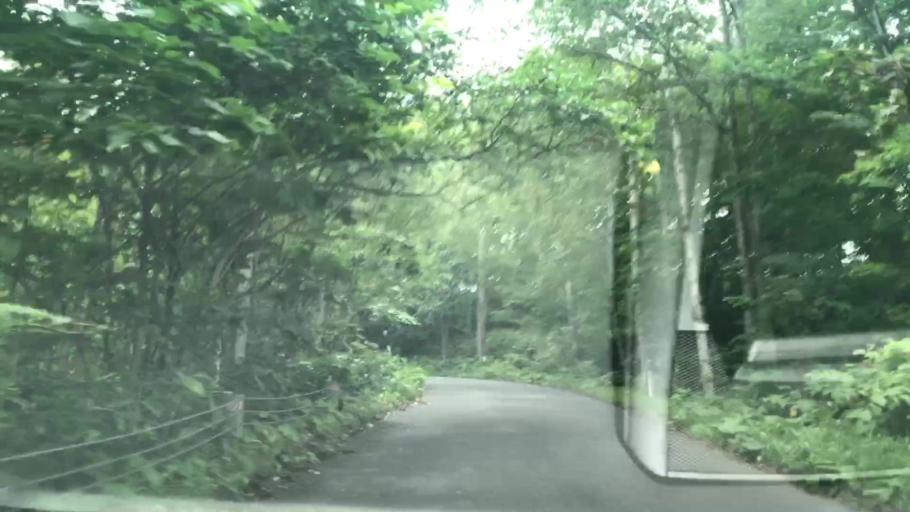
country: JP
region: Hokkaido
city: Yoichi
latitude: 43.1368
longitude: 140.8209
